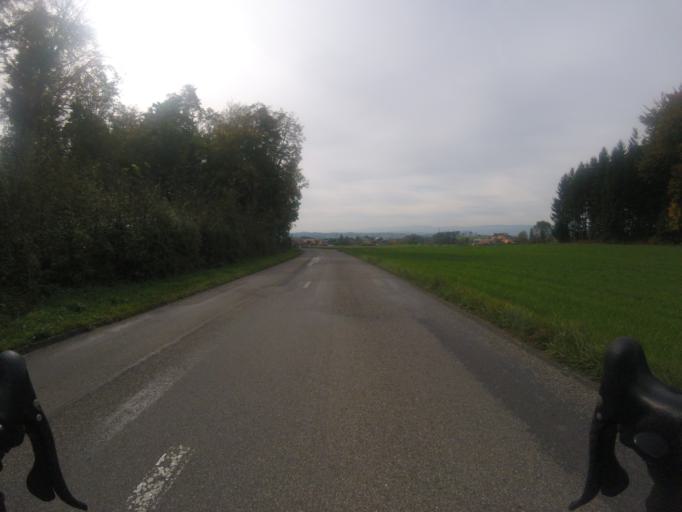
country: CH
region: Bern
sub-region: Bern-Mittelland District
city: Muhleberg
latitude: 46.9484
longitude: 7.2778
